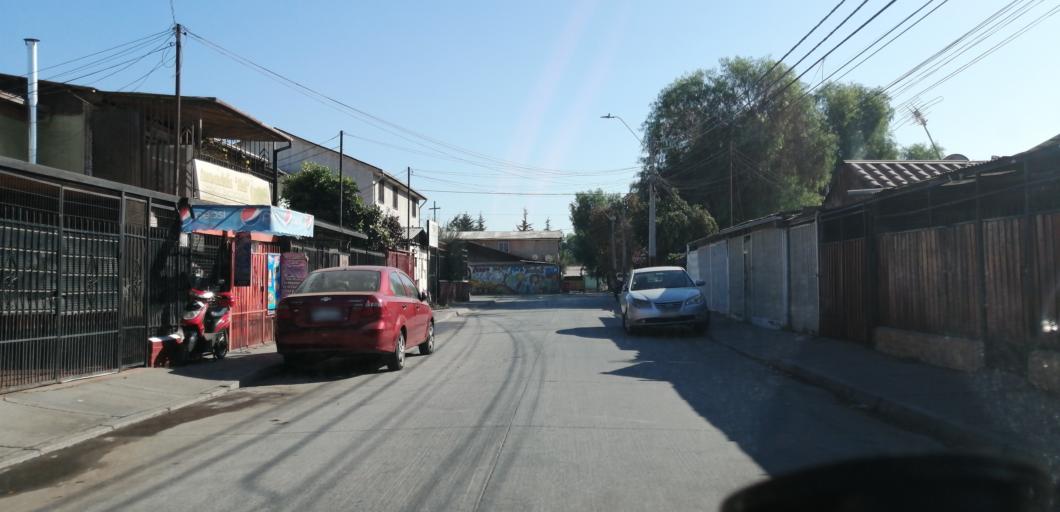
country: CL
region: Santiago Metropolitan
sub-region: Provincia de Santiago
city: Lo Prado
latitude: -33.4306
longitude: -70.7559
